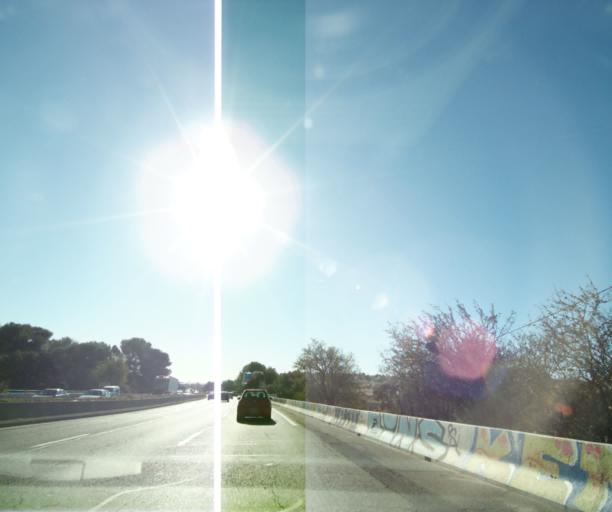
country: FR
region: Provence-Alpes-Cote d'Azur
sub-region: Departement des Bouches-du-Rhone
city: Marseille 15
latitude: 43.3845
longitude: 5.3508
